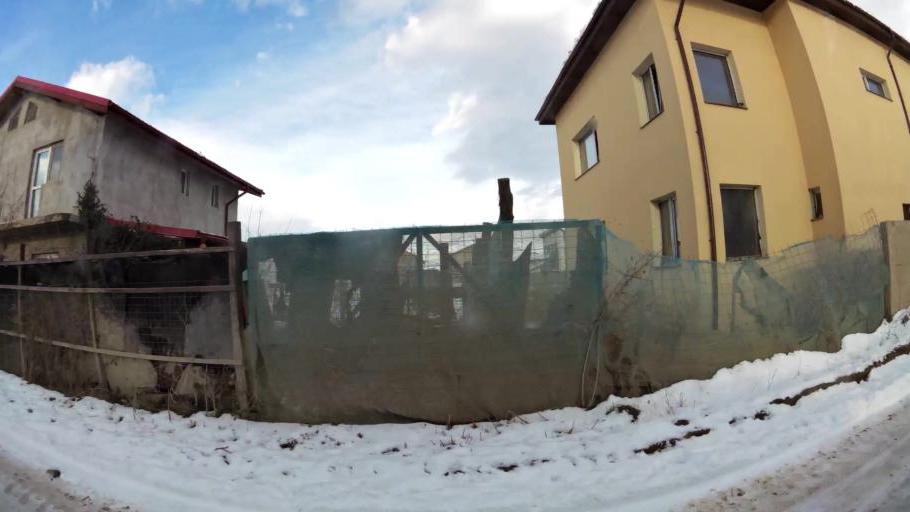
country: RO
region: Ilfov
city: Dobroesti
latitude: 44.4642
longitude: 26.1798
